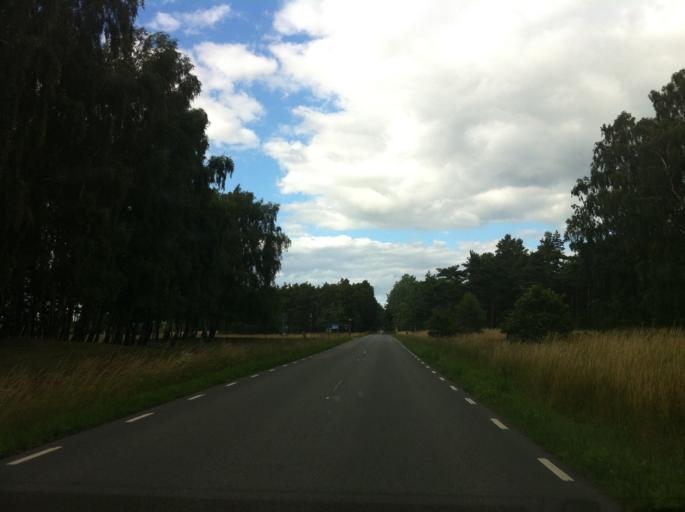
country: SE
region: Skane
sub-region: Simrishamns Kommun
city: Simrishamn
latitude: 55.4111
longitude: 14.1951
